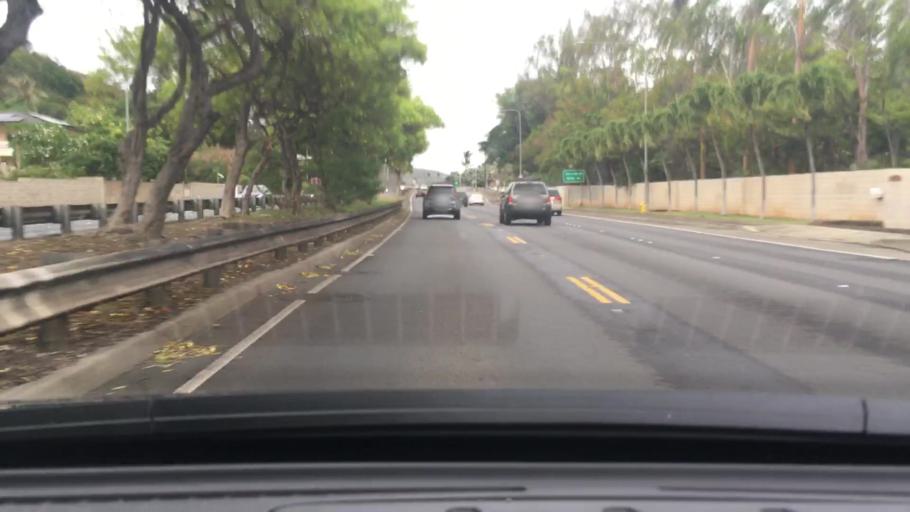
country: US
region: Hawaii
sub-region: Honolulu County
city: Waimanalo
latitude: 21.2791
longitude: -157.7473
